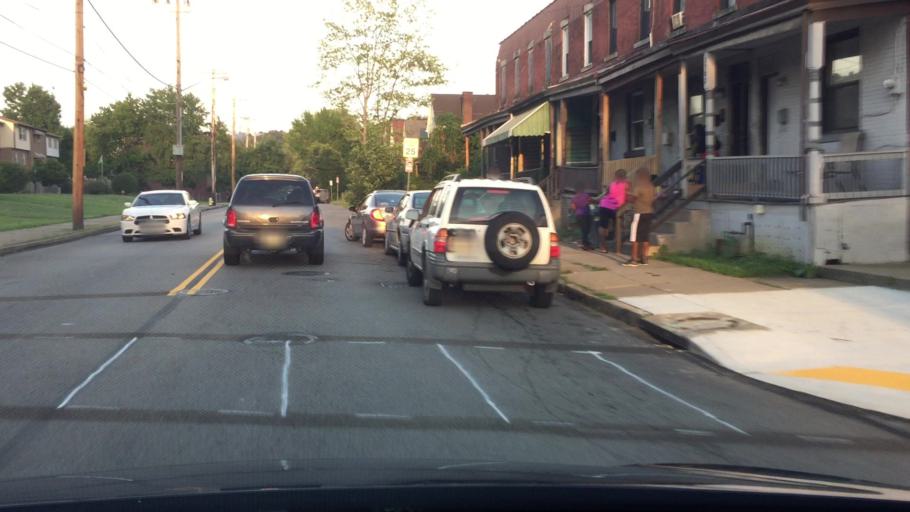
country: US
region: Pennsylvania
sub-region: Allegheny County
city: Wilkinsburg
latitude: 40.4560
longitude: -79.8945
